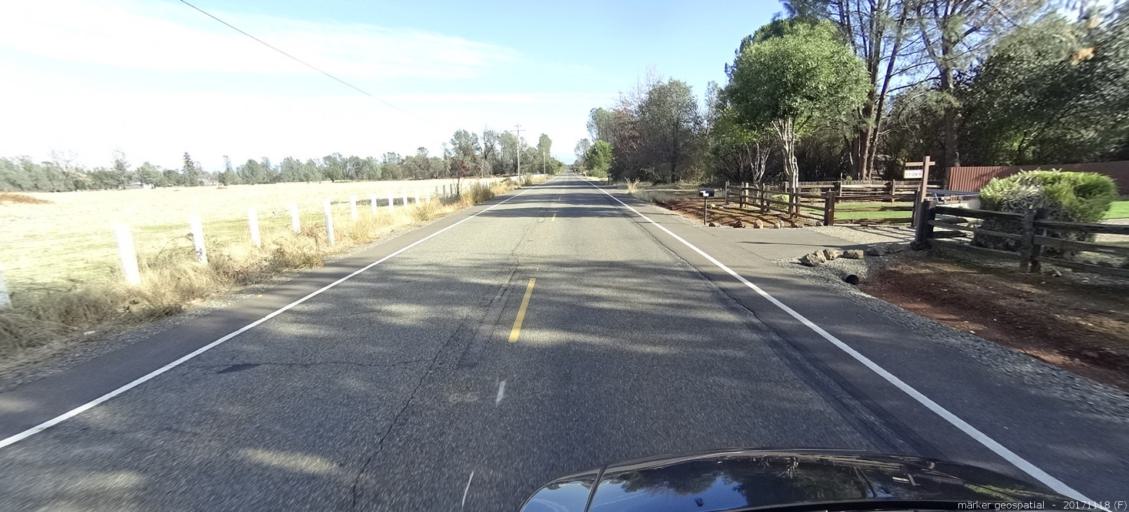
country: US
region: California
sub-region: Shasta County
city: Redding
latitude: 40.4780
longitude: -122.4159
